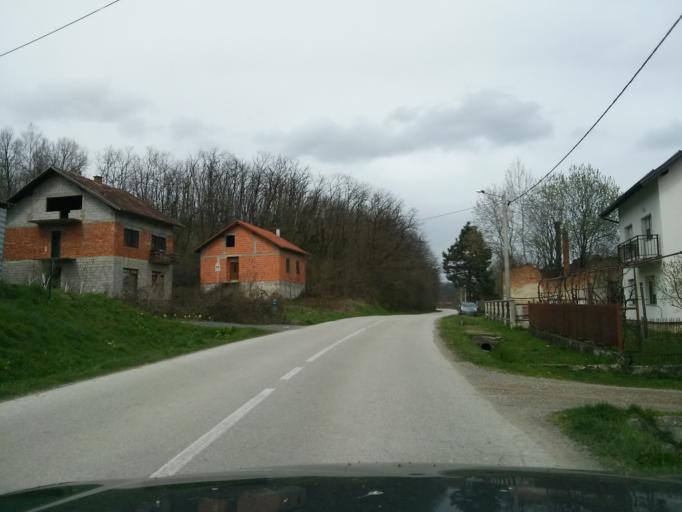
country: HR
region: Sisacko-Moslavacka
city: Gvozd
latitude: 45.2786
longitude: 15.9702
